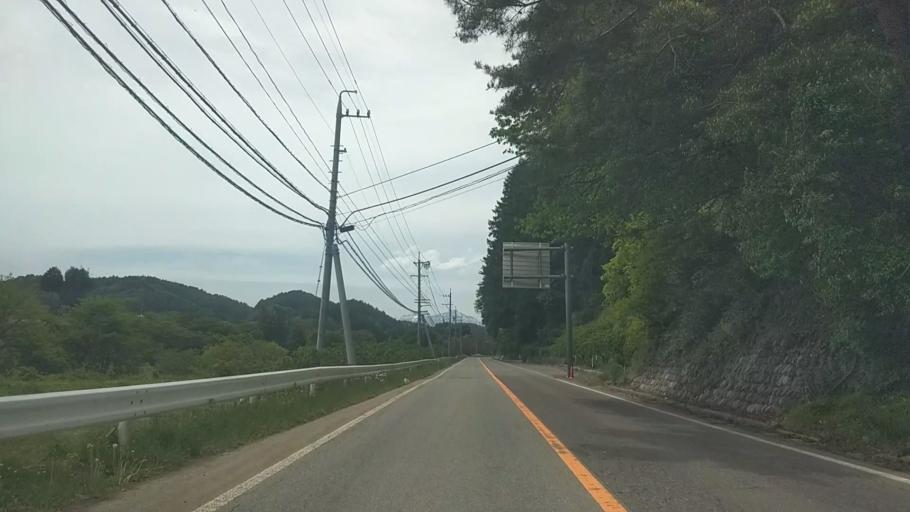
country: JP
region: Nagano
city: Saku
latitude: 36.1271
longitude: 138.4568
